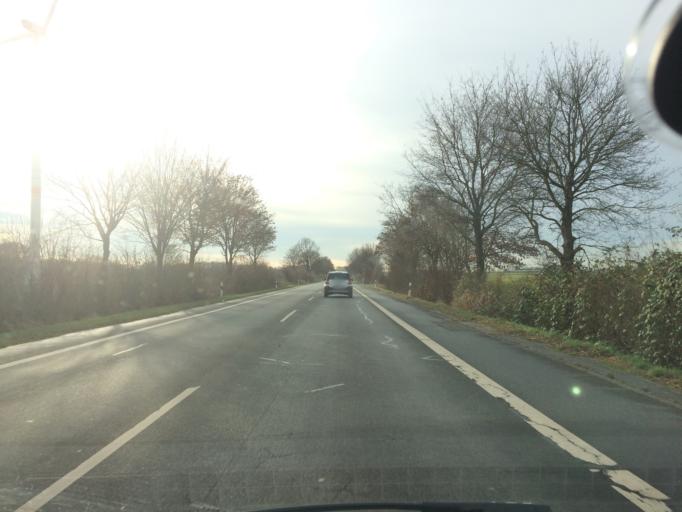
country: DE
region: North Rhine-Westphalia
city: Dorsten
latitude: 51.6266
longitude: 6.9561
